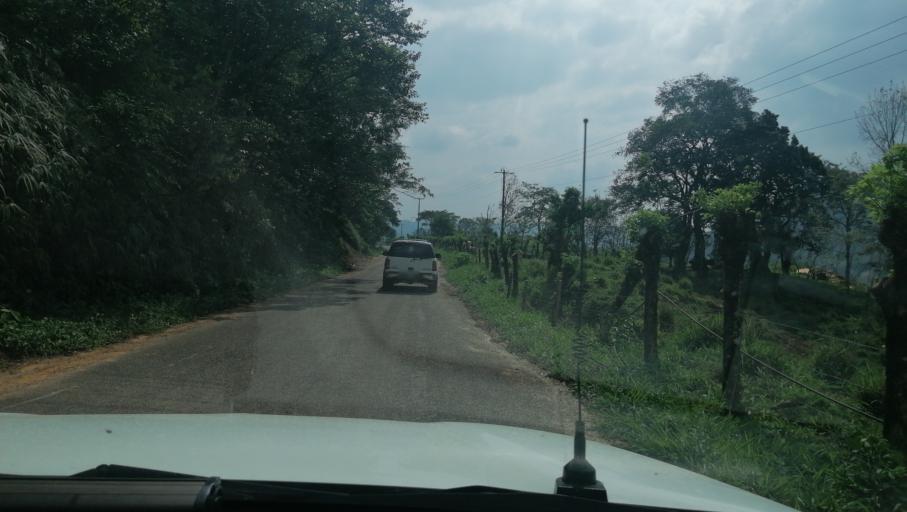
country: MX
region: Chiapas
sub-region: Francisco Leon
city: San Miguel la Sardina
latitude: 17.2321
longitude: -93.3425
